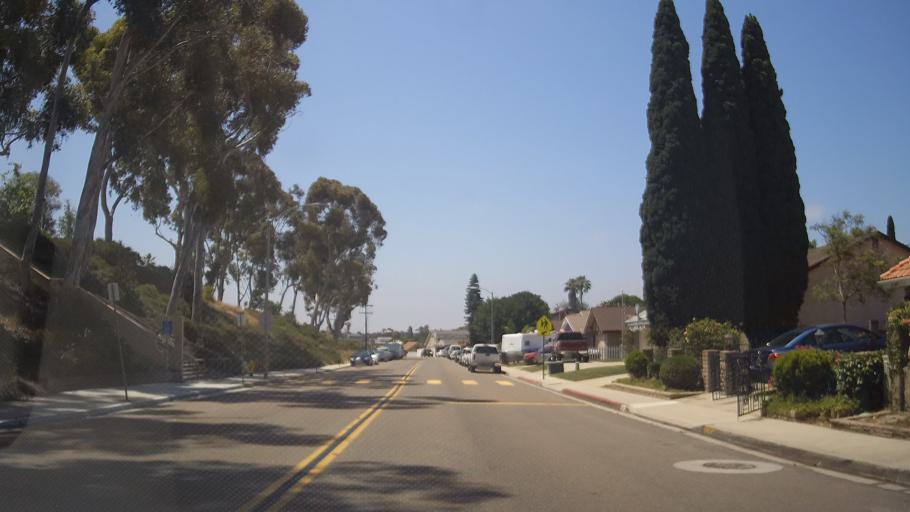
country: US
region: California
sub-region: San Diego County
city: Bonita
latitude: 32.6748
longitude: -117.0485
